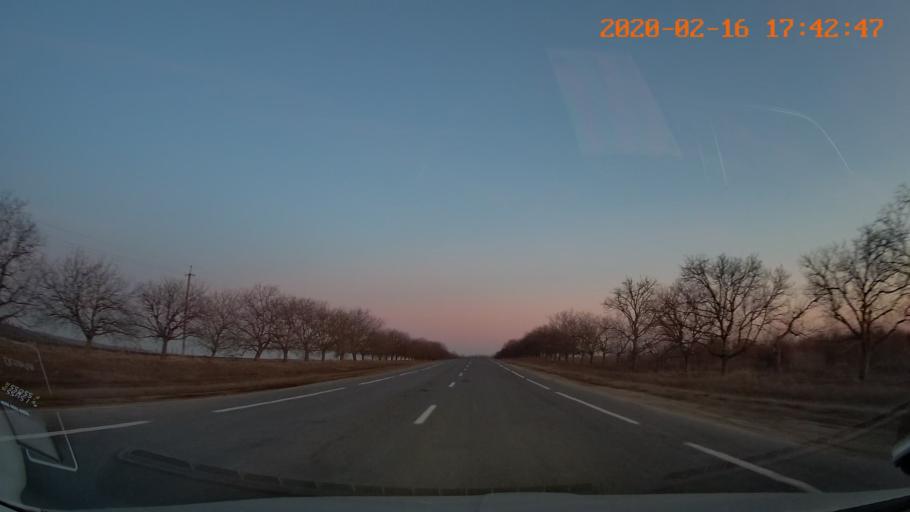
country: MD
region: Riscani
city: Riscani
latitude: 48.0204
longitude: 27.5558
